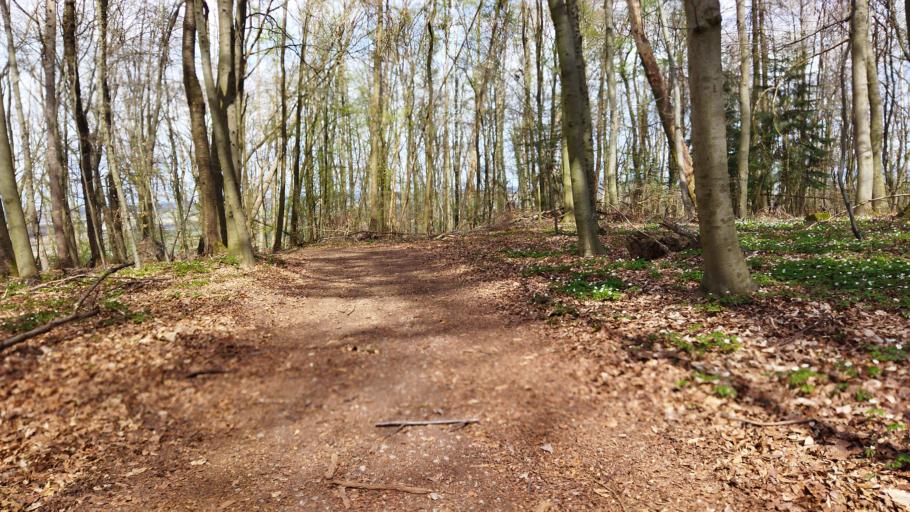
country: DE
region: Baden-Wuerttemberg
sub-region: Regierungsbezirk Stuttgart
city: Eberstadt
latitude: 49.2048
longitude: 9.3033
